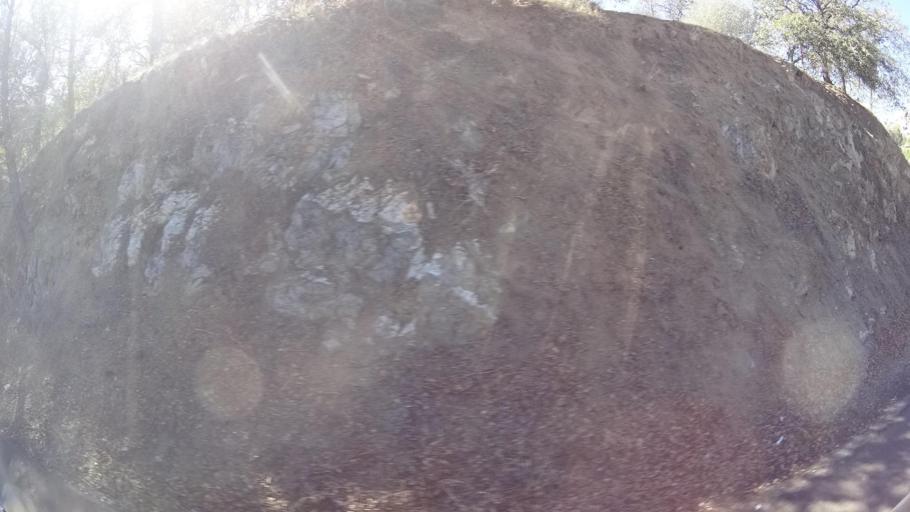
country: US
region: California
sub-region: Kern County
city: Bodfish
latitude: 35.5912
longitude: -118.4983
